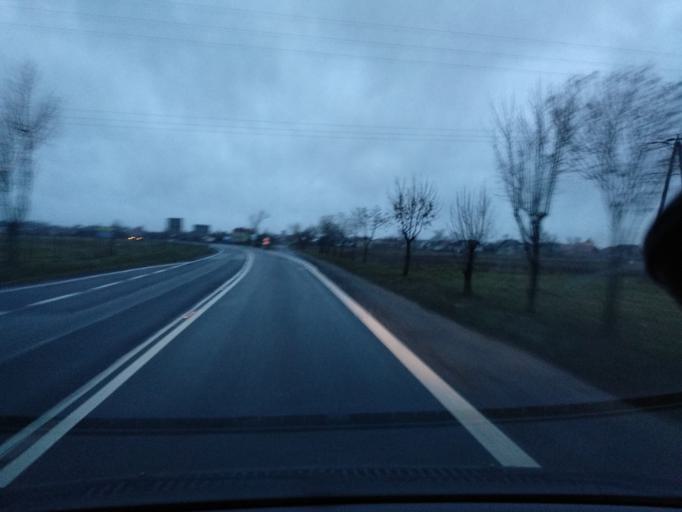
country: PL
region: Lower Silesian Voivodeship
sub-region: Powiat legnicki
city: Prochowice
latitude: 51.2682
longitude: 16.3757
